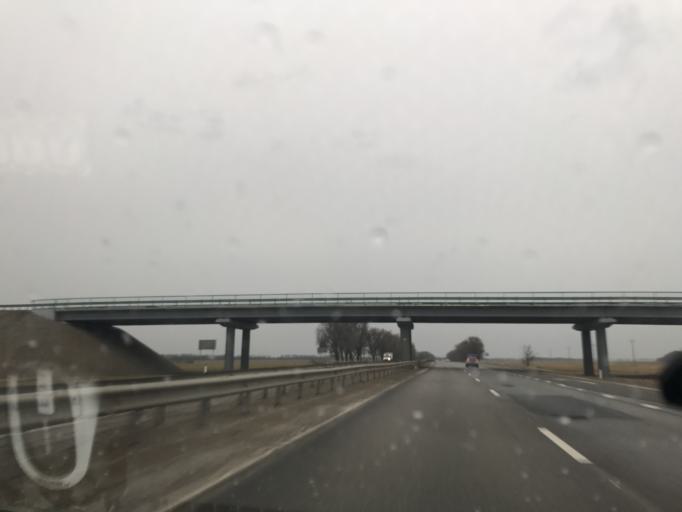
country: RU
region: Krasnodarskiy
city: Pavlovskaya
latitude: 46.1621
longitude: 39.8434
